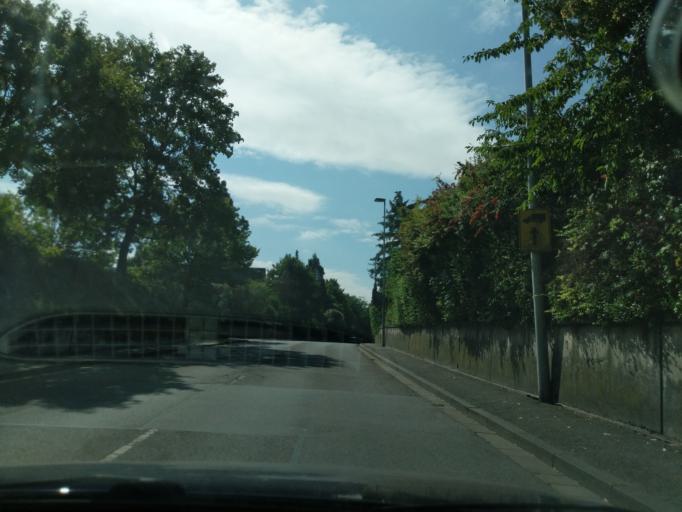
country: DE
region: Rheinland-Pfalz
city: Mainz
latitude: 49.9690
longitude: 8.2819
